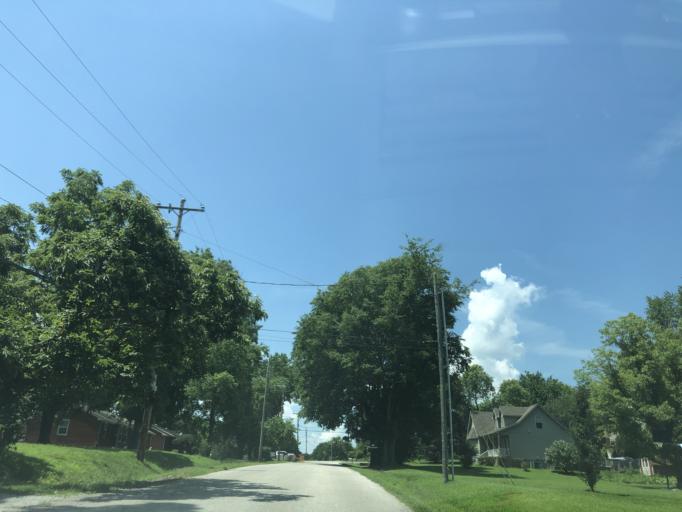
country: US
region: Tennessee
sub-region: Davidson County
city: Lakewood
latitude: 36.1735
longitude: -86.6502
